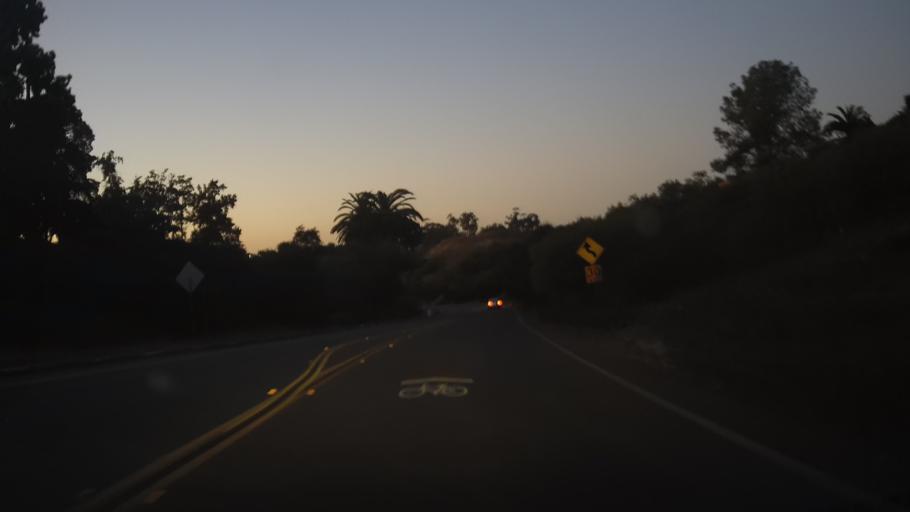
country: US
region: California
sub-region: San Diego County
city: San Diego
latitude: 32.7204
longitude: -117.1385
